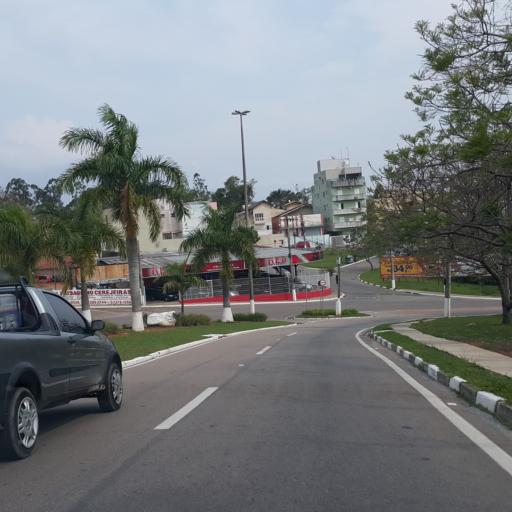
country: BR
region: Sao Paulo
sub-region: Louveira
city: Louveira
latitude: -23.0759
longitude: -46.9527
